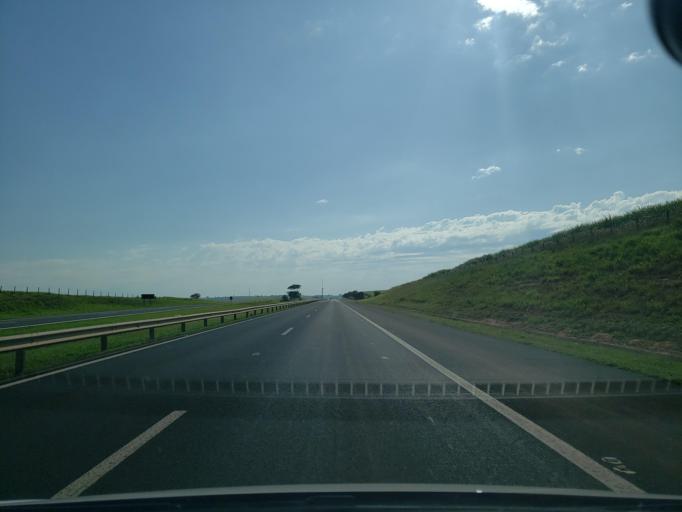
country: BR
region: Sao Paulo
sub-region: Promissao
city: Promissao
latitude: -21.5420
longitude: -49.9686
